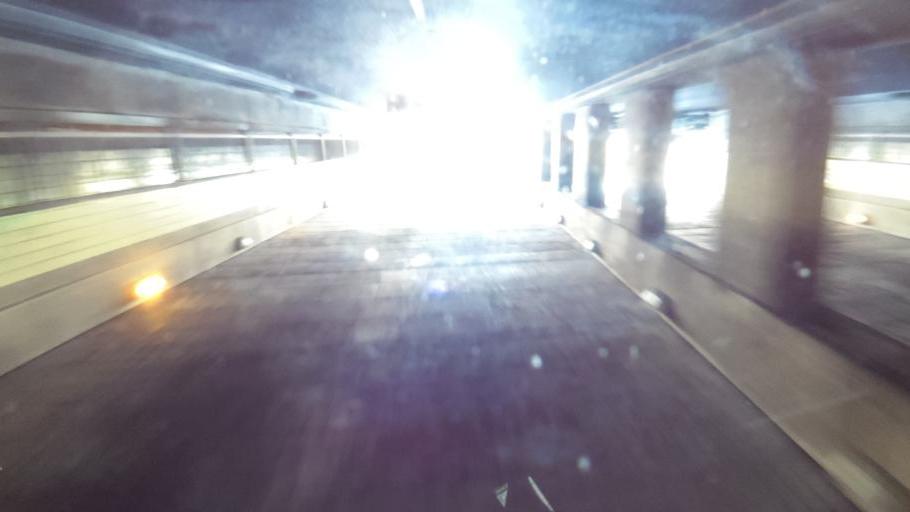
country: CA
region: Ontario
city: Etobicoke
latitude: 43.6667
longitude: -79.4916
